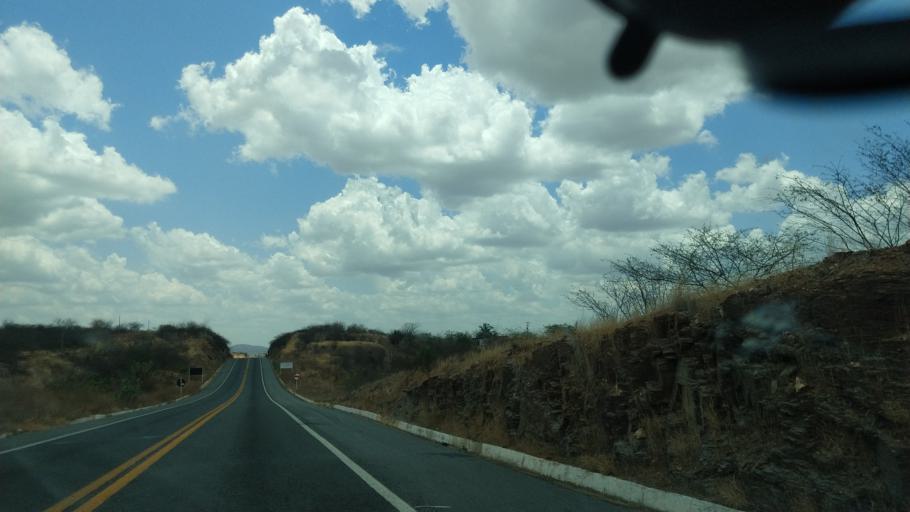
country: BR
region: Rio Grande do Norte
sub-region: Currais Novos
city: Currais Novos
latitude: -6.2561
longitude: -36.4867
